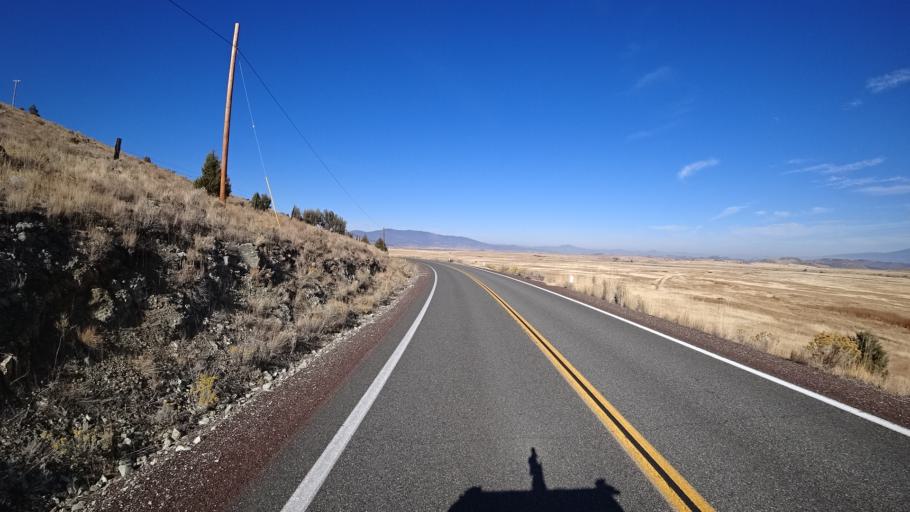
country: US
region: California
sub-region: Siskiyou County
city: Weed
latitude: 41.4667
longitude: -122.4667
